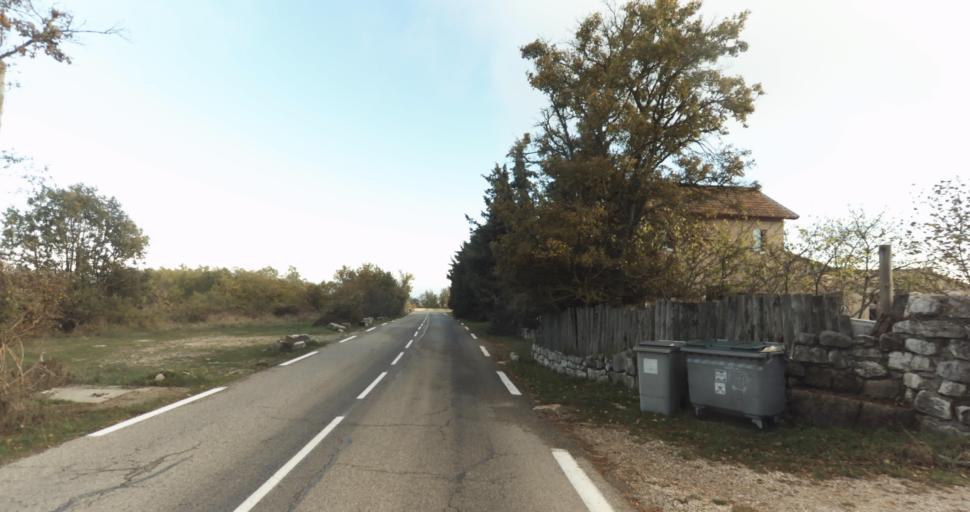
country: FR
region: Provence-Alpes-Cote d'Azur
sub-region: Departement des Alpes-Maritimes
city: Tourrettes-sur-Loup
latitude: 43.7595
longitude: 7.0759
